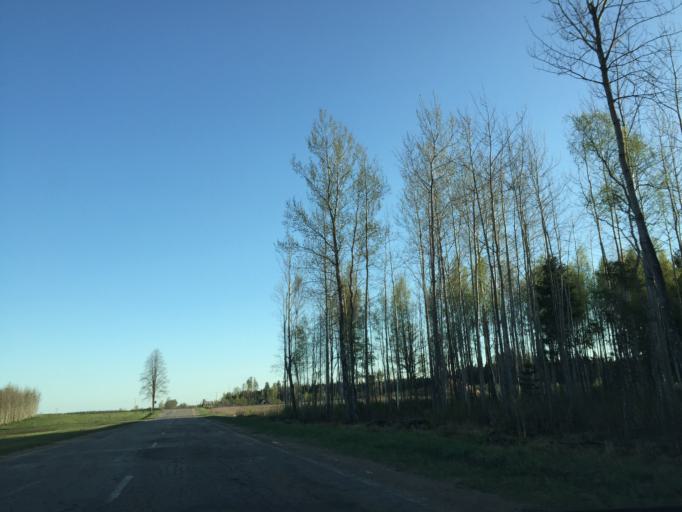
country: LV
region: Koknese
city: Koknese
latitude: 56.6960
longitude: 25.4873
